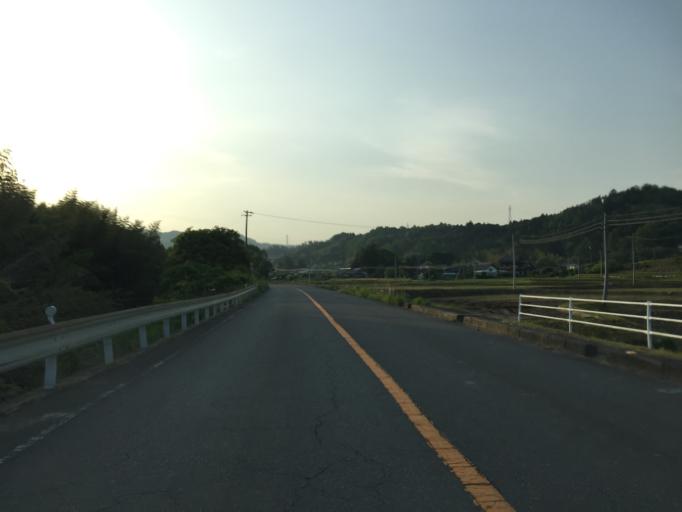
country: JP
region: Fukushima
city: Iwaki
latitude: 37.2112
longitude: 140.9857
